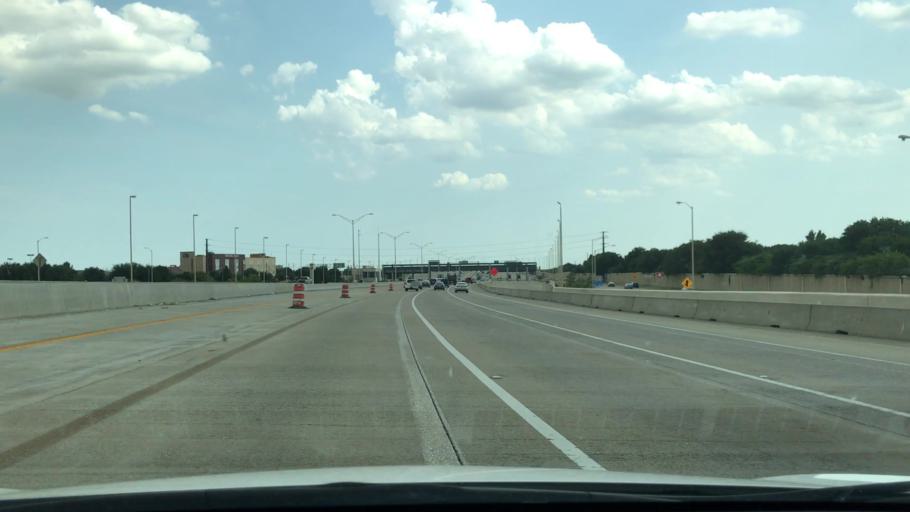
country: US
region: Texas
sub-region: Collin County
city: Plano
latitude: 32.9940
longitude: -96.6689
